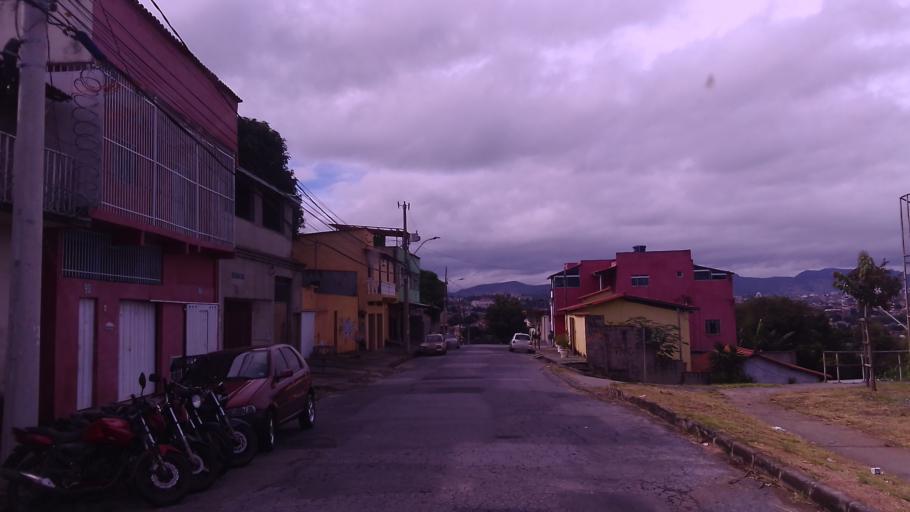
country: BR
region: Minas Gerais
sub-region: Santa Luzia
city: Santa Luzia
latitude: -19.8371
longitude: -43.9001
